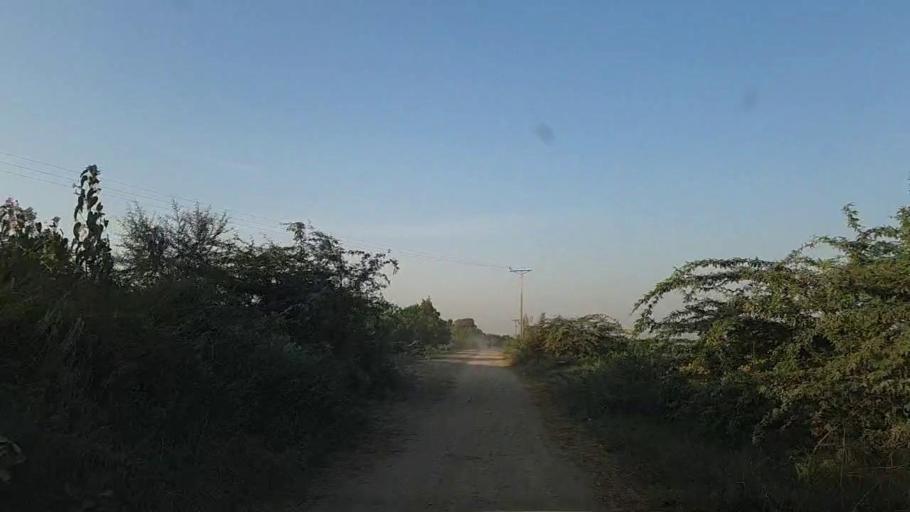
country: PK
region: Sindh
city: Mirpur Batoro
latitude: 24.7212
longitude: 68.2140
